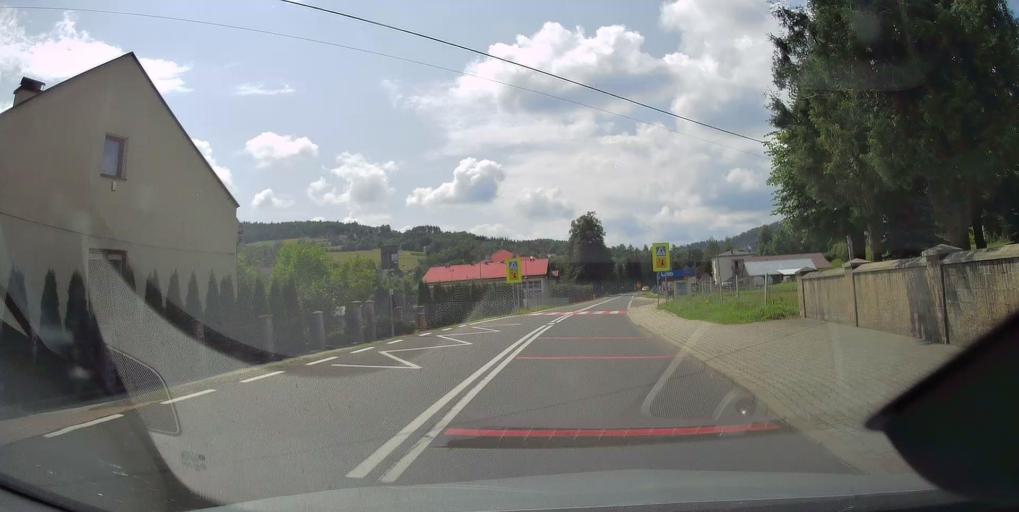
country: PL
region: Lesser Poland Voivodeship
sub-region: Powiat tarnowski
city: Zakliczyn
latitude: 49.7946
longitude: 20.8006
